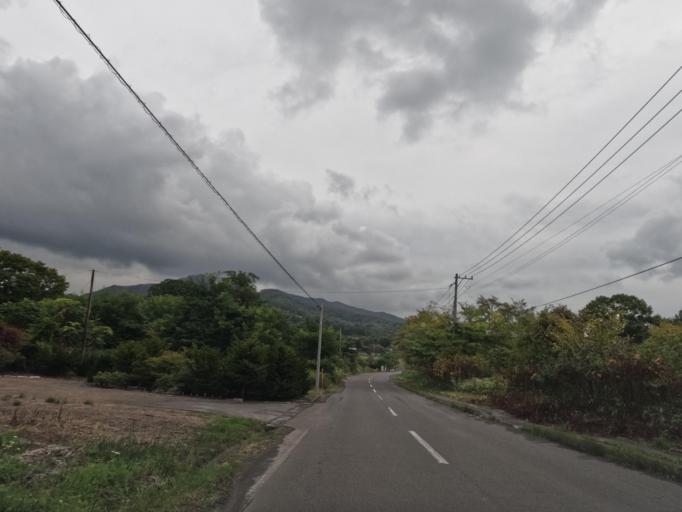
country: JP
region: Hokkaido
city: Date
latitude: 42.4551
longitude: 140.9041
